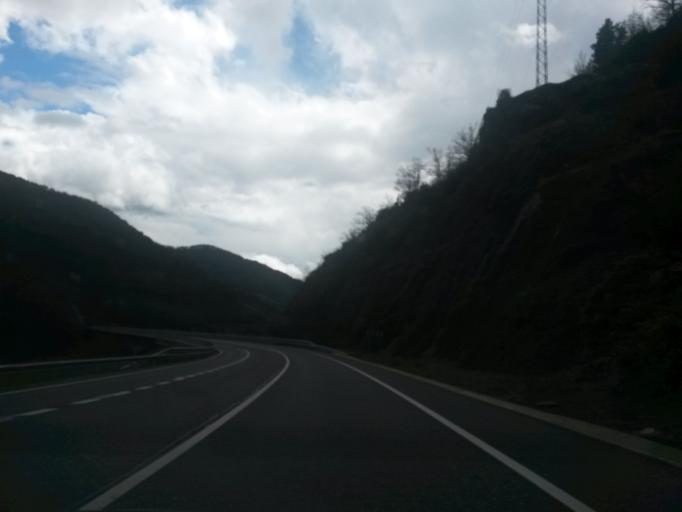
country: ES
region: Catalonia
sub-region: Provincia de Barcelona
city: Baga
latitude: 42.2843
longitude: 1.8500
